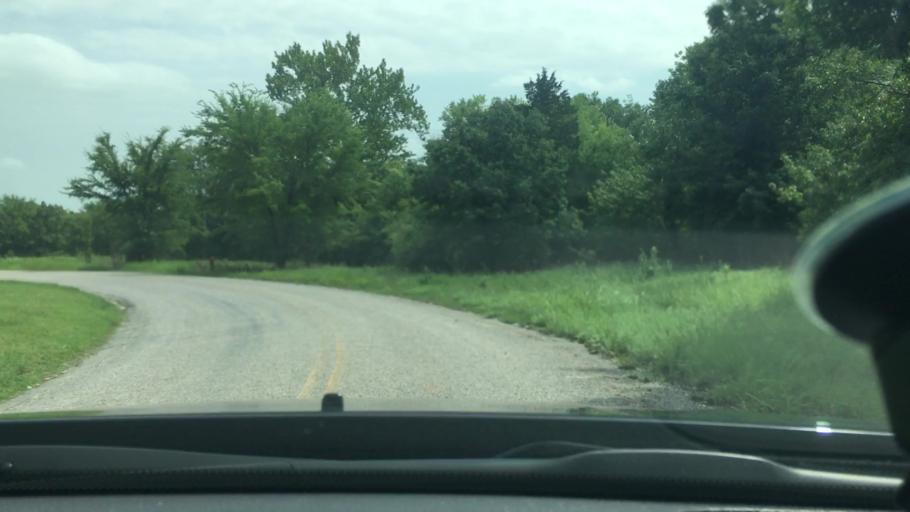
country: US
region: Oklahoma
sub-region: Pontotoc County
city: Ada
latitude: 34.8137
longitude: -96.7116
